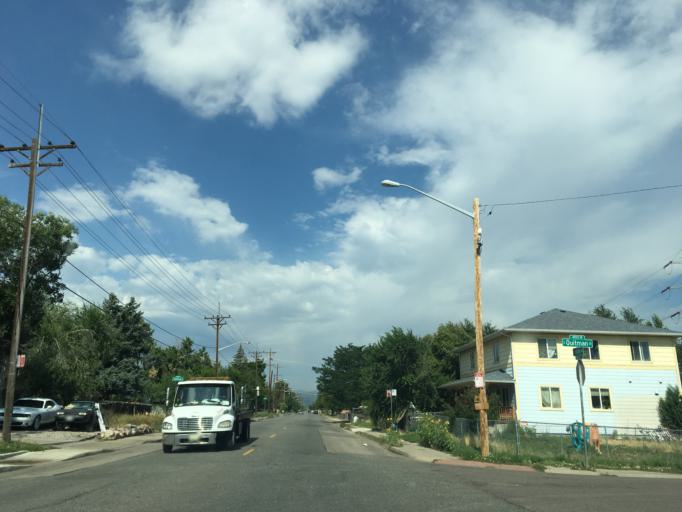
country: US
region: Colorado
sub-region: Jefferson County
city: Lakewood
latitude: 39.7004
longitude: -105.0406
